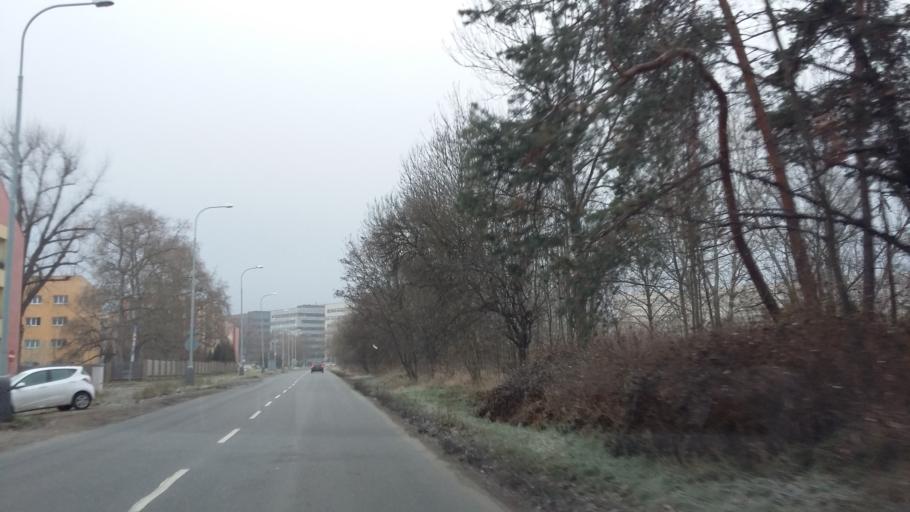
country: CZ
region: Praha
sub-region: Praha 9
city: Prosek
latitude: 50.1187
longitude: 14.5073
